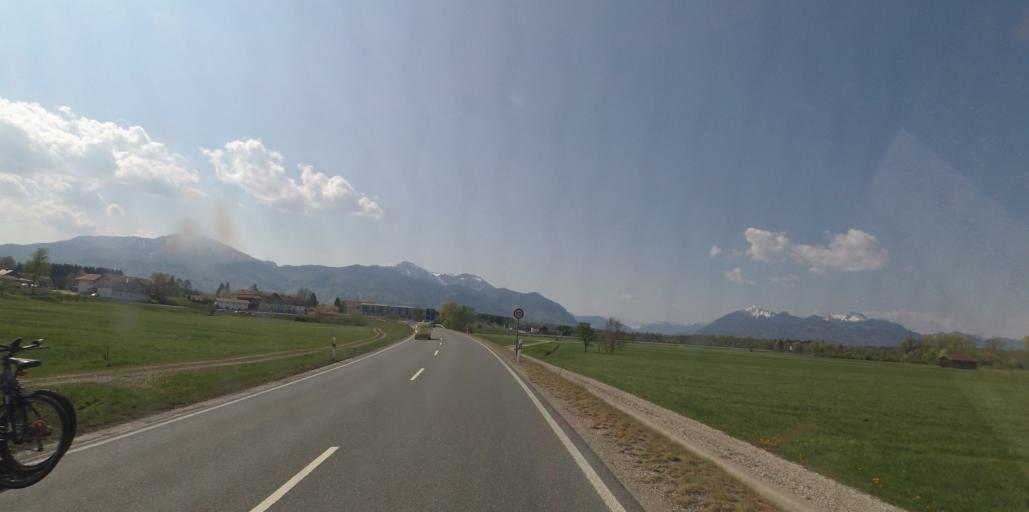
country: DE
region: Bavaria
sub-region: Upper Bavaria
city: Grabenstatt
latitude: 47.8344
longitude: 12.5242
